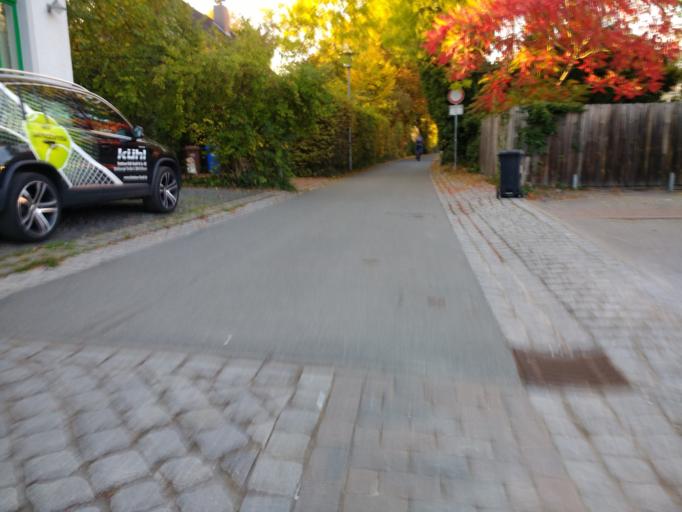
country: DE
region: Lower Saxony
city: Gifhorn
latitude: 52.4864
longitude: 10.5446
